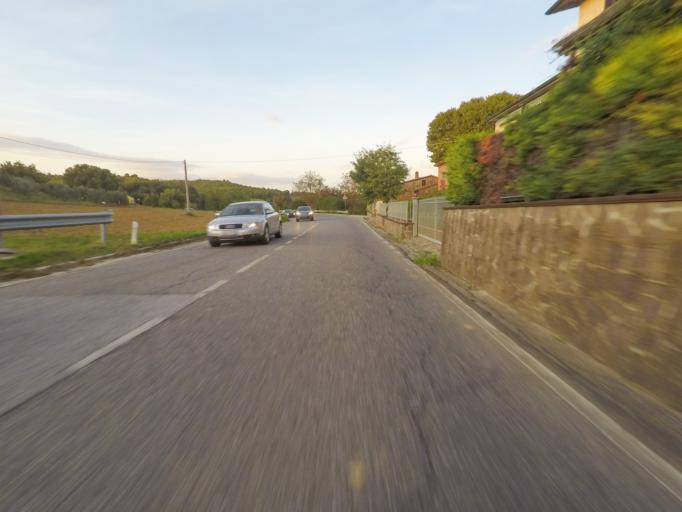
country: IT
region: Tuscany
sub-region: Provincia di Siena
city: Montepulciano
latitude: 43.1324
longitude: 11.7296
